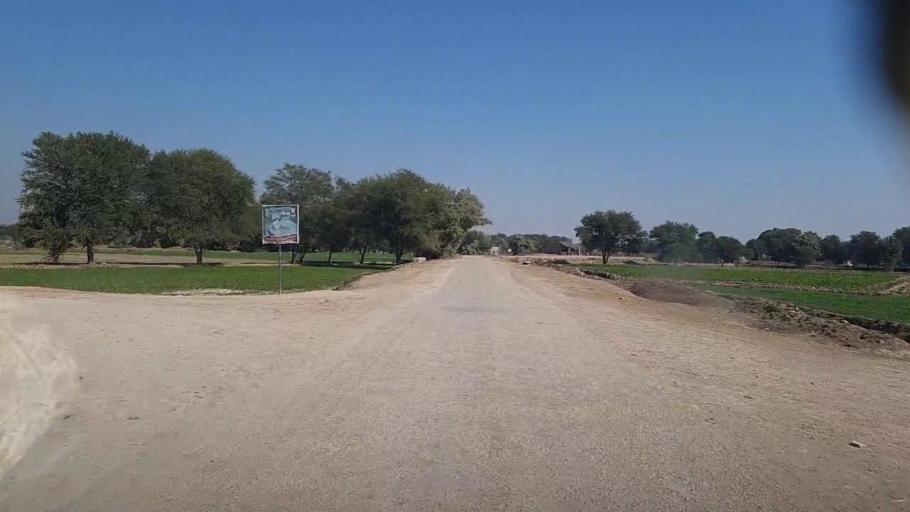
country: PK
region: Sindh
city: Khairpur
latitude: 27.9775
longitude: 69.8371
